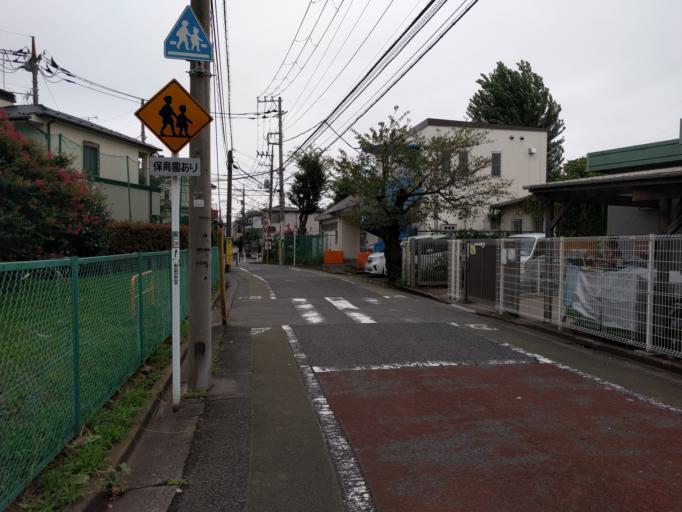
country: JP
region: Tokyo
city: Tokyo
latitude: 35.6270
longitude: 139.6527
